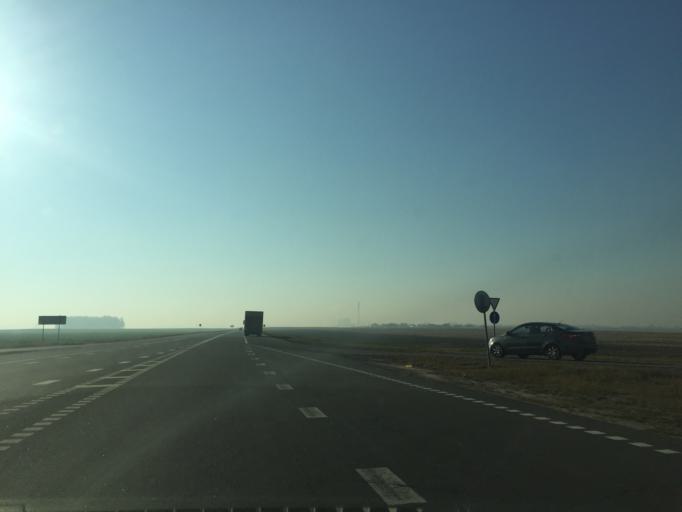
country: BY
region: Gomel
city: Kastsyukowka
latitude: 52.4878
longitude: 30.8189
